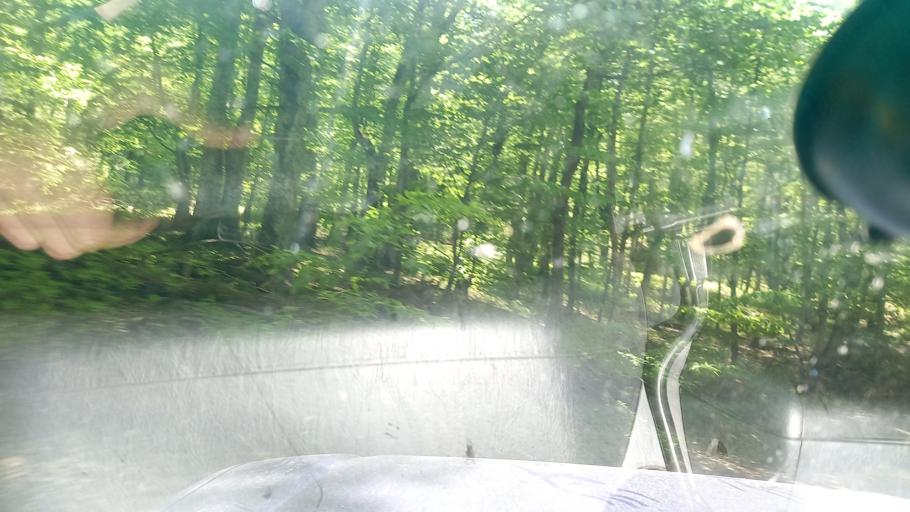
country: RU
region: Krasnodarskiy
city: Tuapse
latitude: 44.2551
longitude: 39.2855
